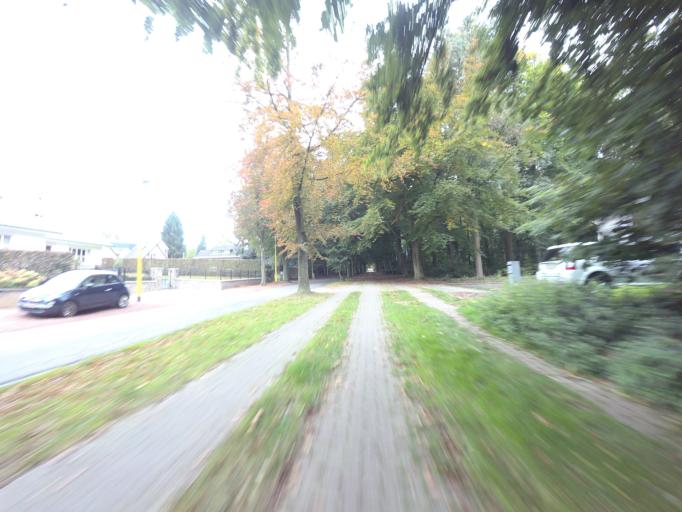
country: BE
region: Flanders
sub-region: Provincie Vlaams-Brabant
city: Grimbergen
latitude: 50.9292
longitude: 4.3734
